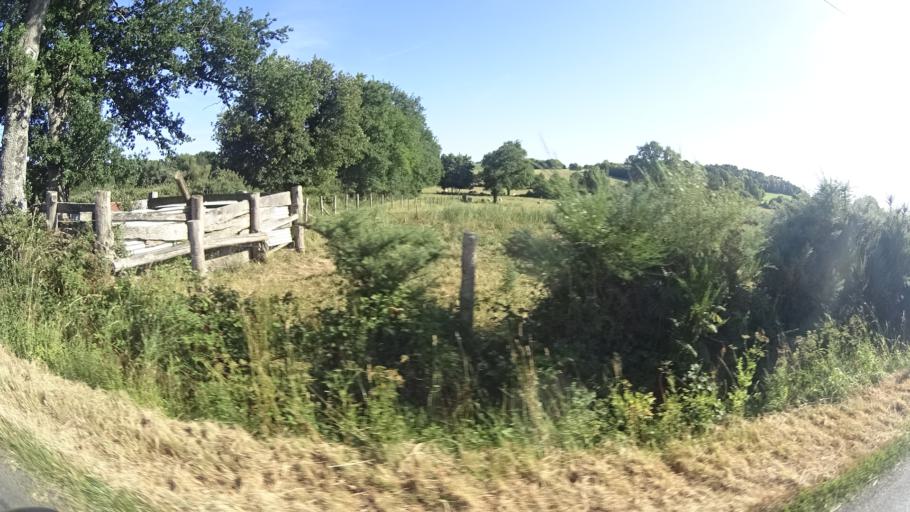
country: FR
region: Brittany
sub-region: Departement d'Ille-et-Vilaine
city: Grand-Fougeray
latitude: 47.7332
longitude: -1.7723
